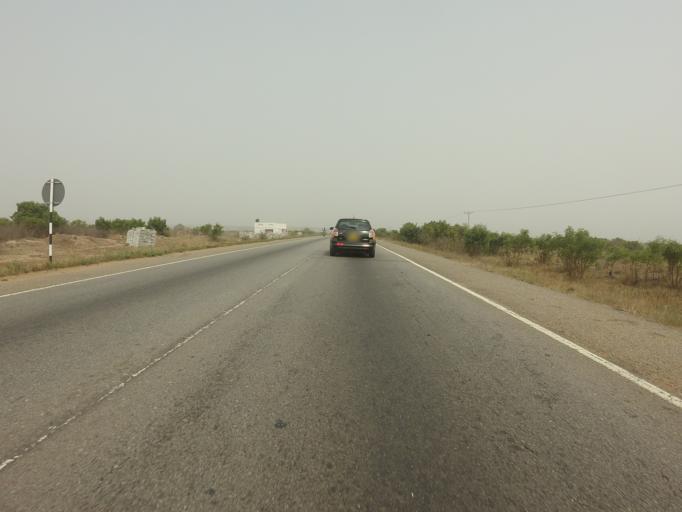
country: GH
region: Greater Accra
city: Tema
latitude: 5.8592
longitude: 0.2741
